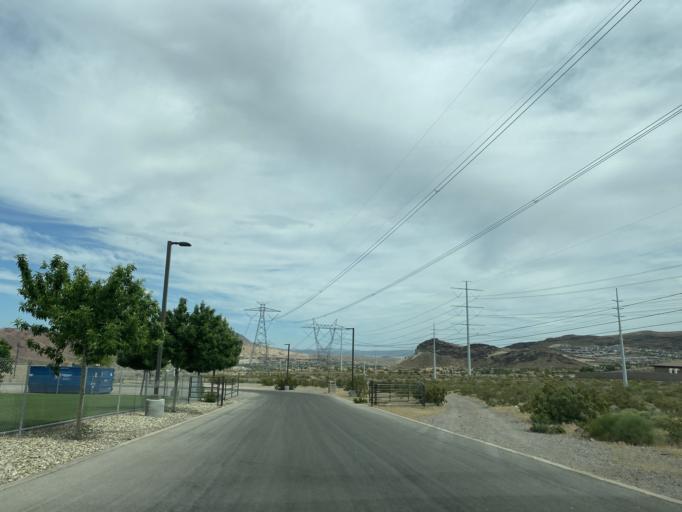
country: US
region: Nevada
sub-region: Clark County
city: Henderson
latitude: 36.0796
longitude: -114.9390
